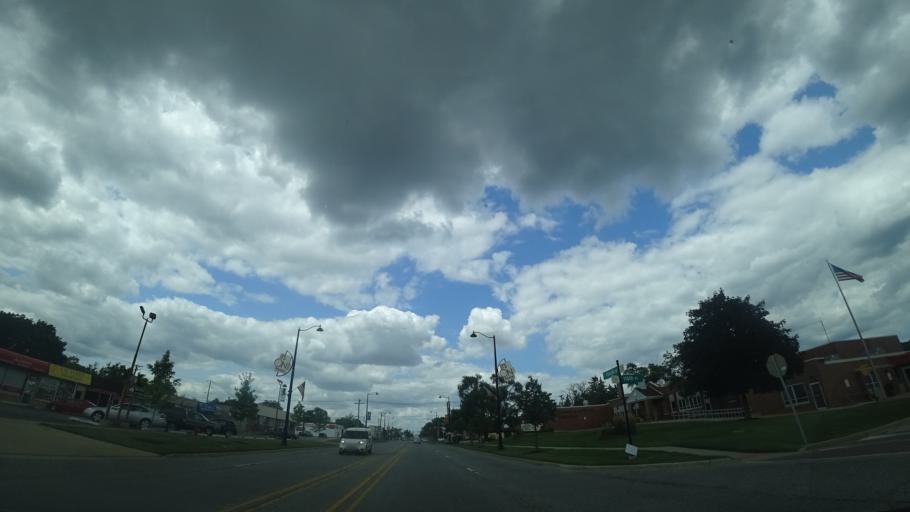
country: US
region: Illinois
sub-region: Cook County
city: Merrionette Park
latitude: 41.6812
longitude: -87.7199
